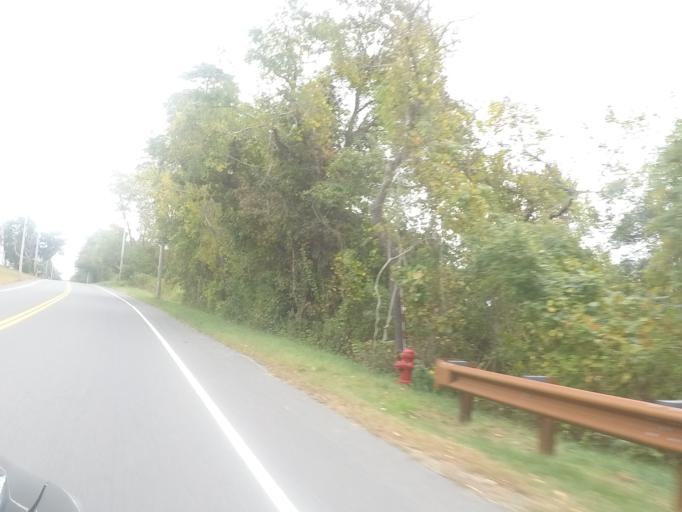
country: US
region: Massachusetts
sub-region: Bristol County
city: Smith Mills
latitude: 41.6781
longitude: -70.9967
